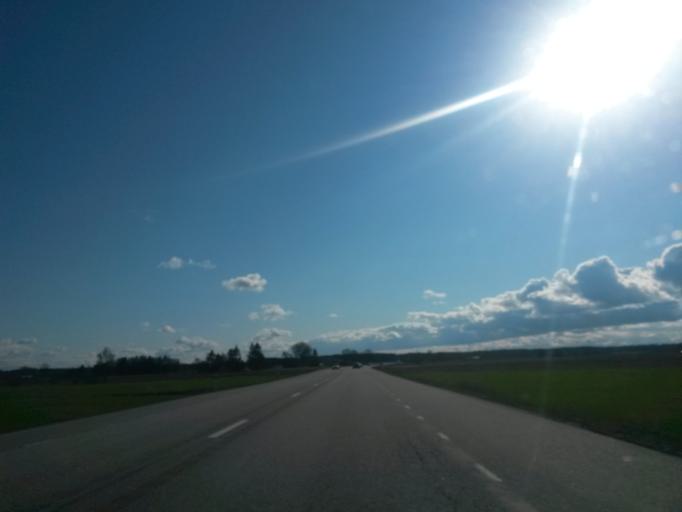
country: SE
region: Vaestra Goetaland
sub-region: Vara Kommun
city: Vara
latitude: 58.2410
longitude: 12.9406
